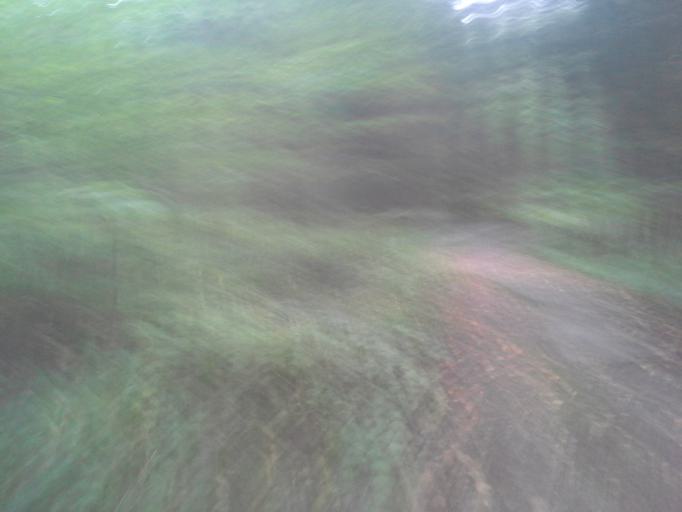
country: RU
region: Moskovskaya
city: Kievskij
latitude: 55.3489
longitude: 36.9299
